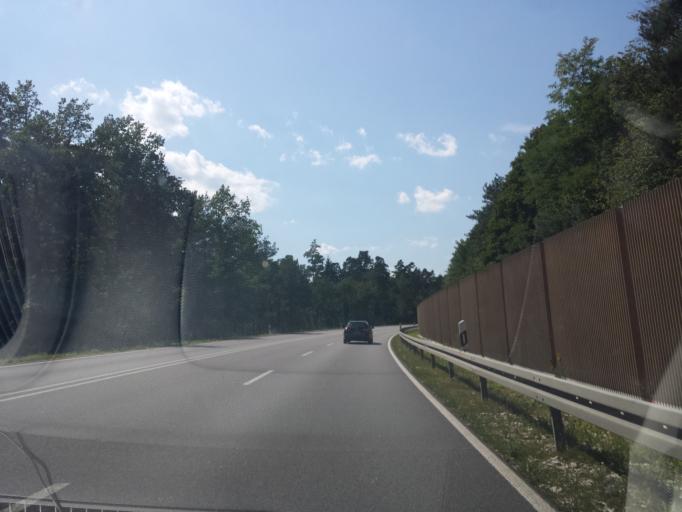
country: DE
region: Bavaria
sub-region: Upper Bavaria
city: Ernsgaden
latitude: 48.7267
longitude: 11.5741
